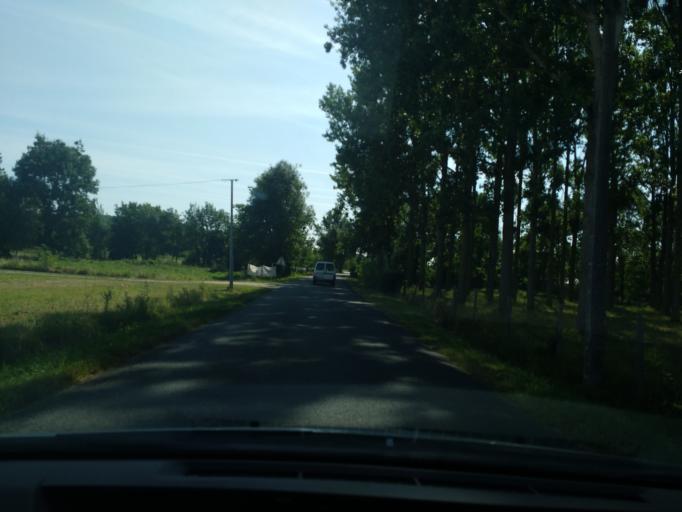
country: FR
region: Pays de la Loire
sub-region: Departement de Maine-et-Loire
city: Beaufort-en-Vallee
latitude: 47.4899
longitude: -0.2007
